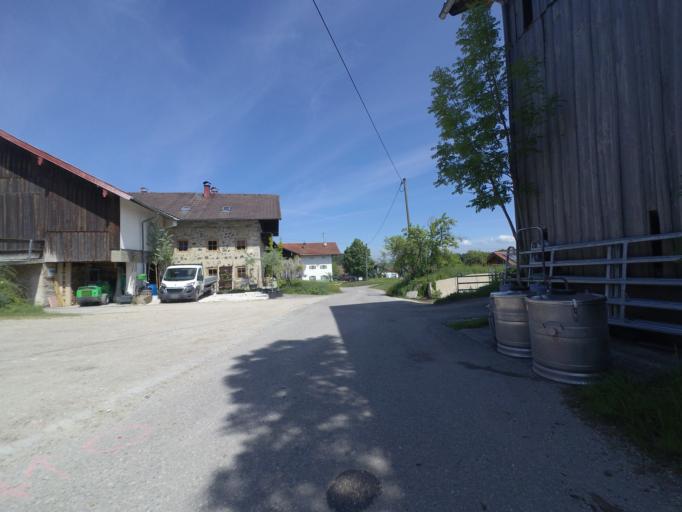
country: DE
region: Bavaria
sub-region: Upper Bavaria
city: Petting
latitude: 47.9048
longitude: 12.8001
